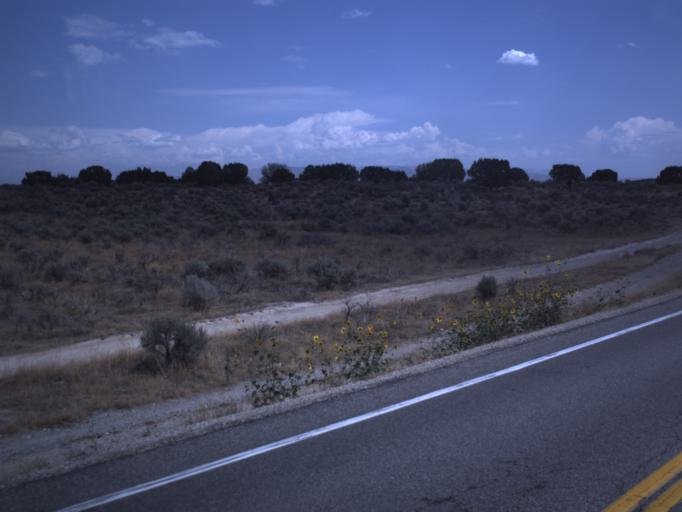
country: US
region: Utah
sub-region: Utah County
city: Eagle Mountain
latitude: 40.2325
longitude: -112.1926
